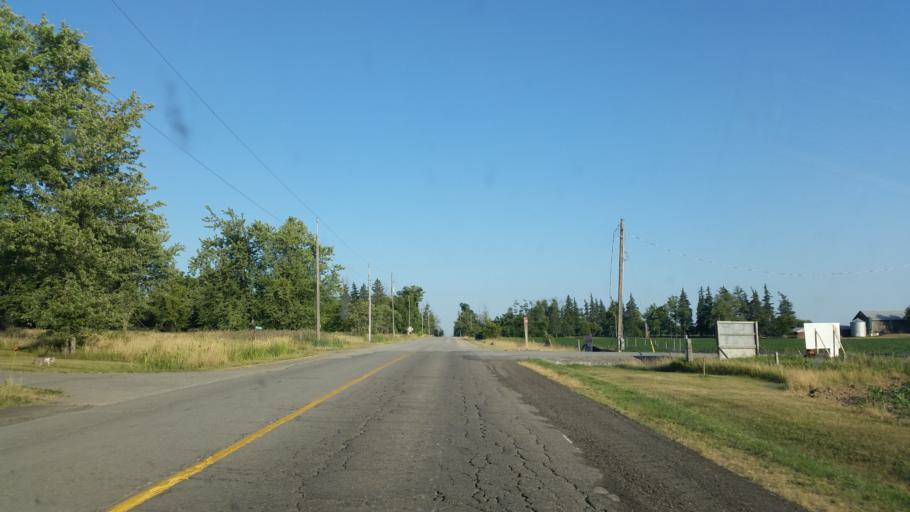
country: CA
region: Ontario
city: Brampton
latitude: 43.7610
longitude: -79.8146
